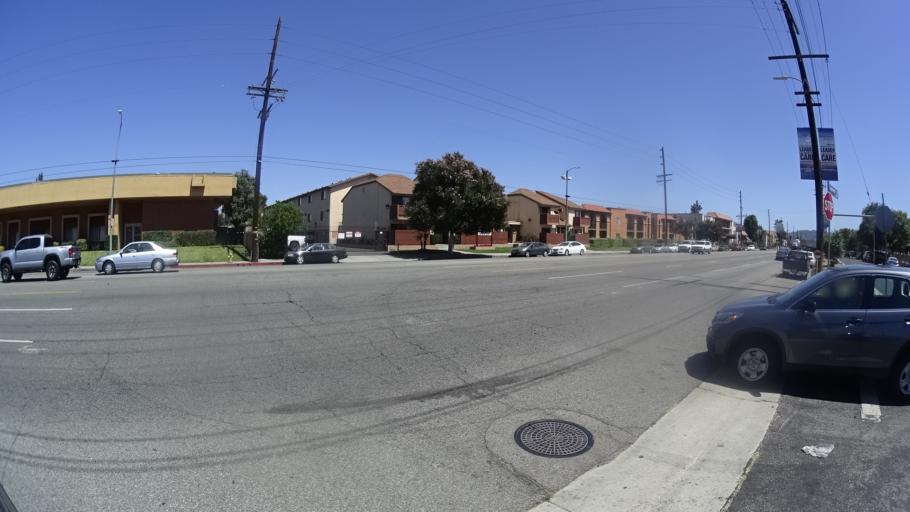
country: US
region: California
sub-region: Los Angeles County
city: Van Nuys
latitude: 34.1922
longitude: -118.4664
